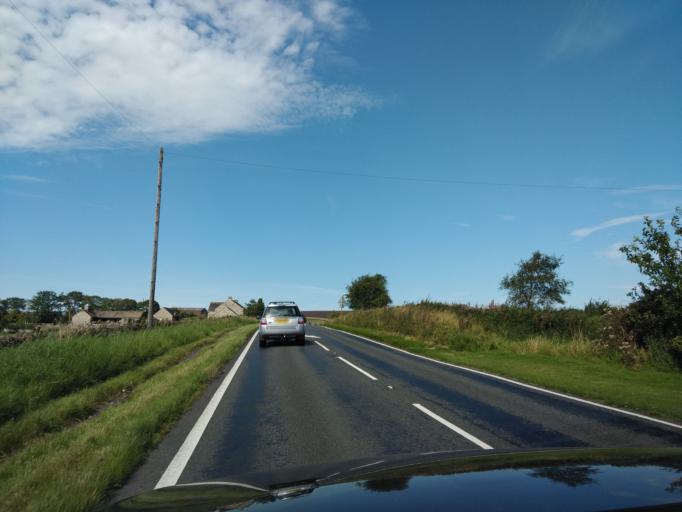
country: GB
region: England
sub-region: Derbyshire
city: Dronfield
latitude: 53.2959
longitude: -1.5479
